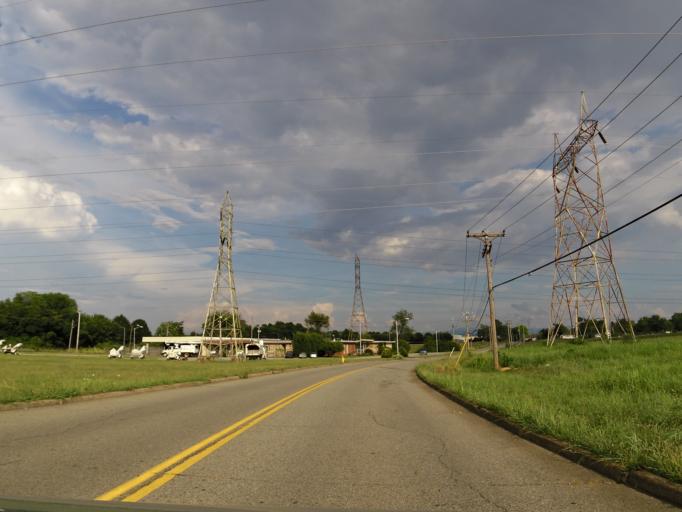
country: US
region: Tennessee
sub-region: Blount County
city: Maryville
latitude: 35.7705
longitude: -83.9790
